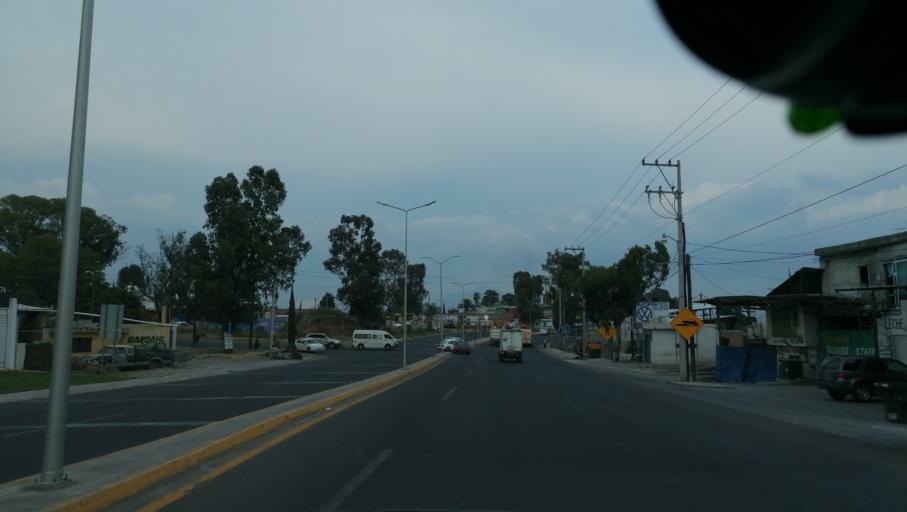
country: MX
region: Puebla
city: Tlazcalancingo
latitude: 19.0219
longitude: -98.3061
